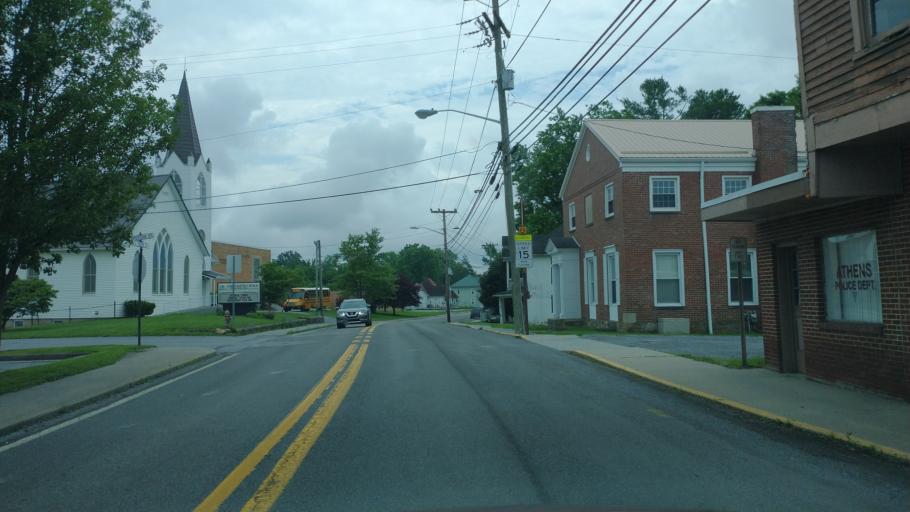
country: US
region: West Virginia
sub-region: Mercer County
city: Athens
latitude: 37.4227
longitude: -81.0161
